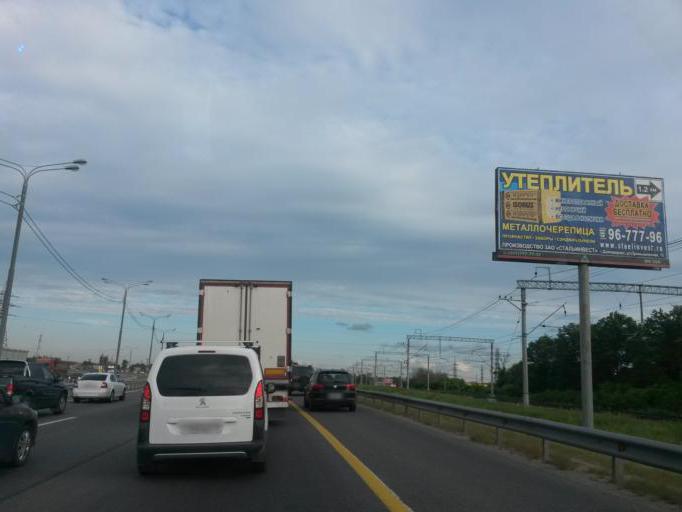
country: RU
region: Moskovskaya
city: Domodedovo
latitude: 55.4651
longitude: 37.7555
